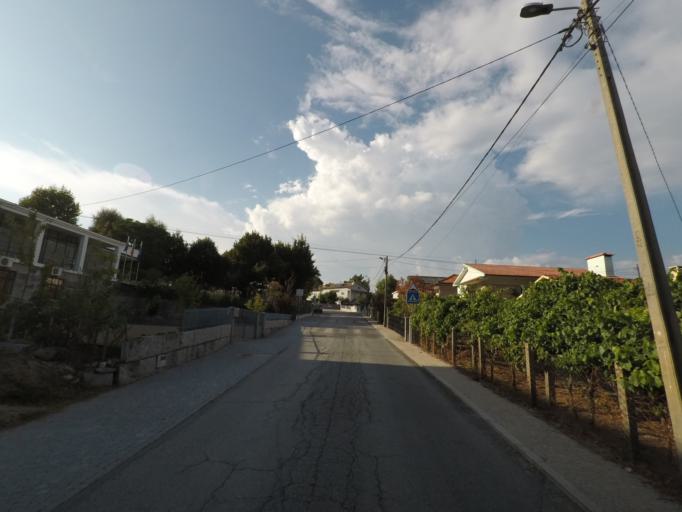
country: PT
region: Porto
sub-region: Baiao
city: Valadares
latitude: 41.1670
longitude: -7.9317
